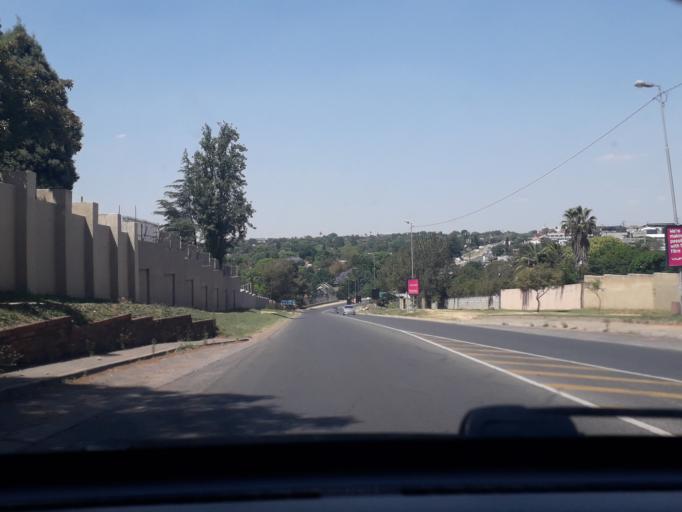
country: ZA
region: Gauteng
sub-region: City of Johannesburg Metropolitan Municipality
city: Modderfontein
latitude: -26.0883
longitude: 28.0697
